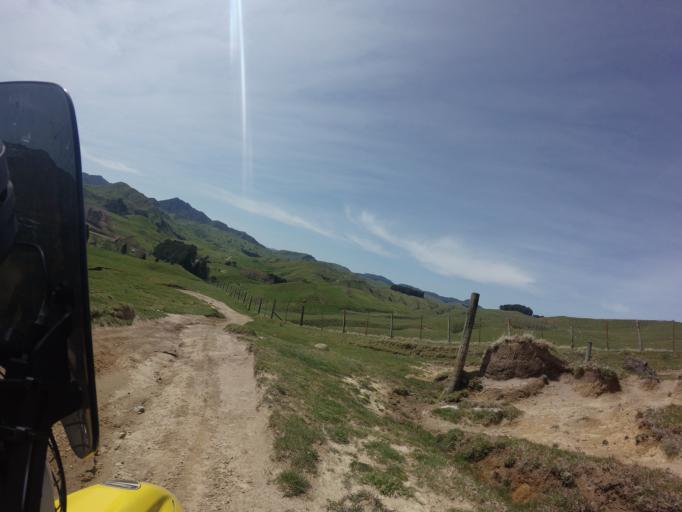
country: NZ
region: Bay of Plenty
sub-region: Opotiki District
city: Opotiki
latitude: -38.4666
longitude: 177.3792
